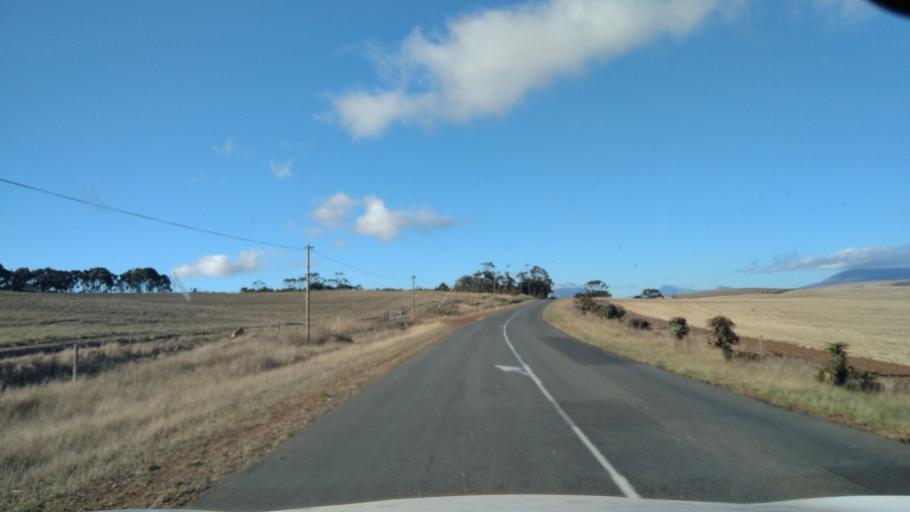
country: ZA
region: Western Cape
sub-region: Overberg District Municipality
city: Caledon
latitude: -34.2049
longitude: 19.2701
